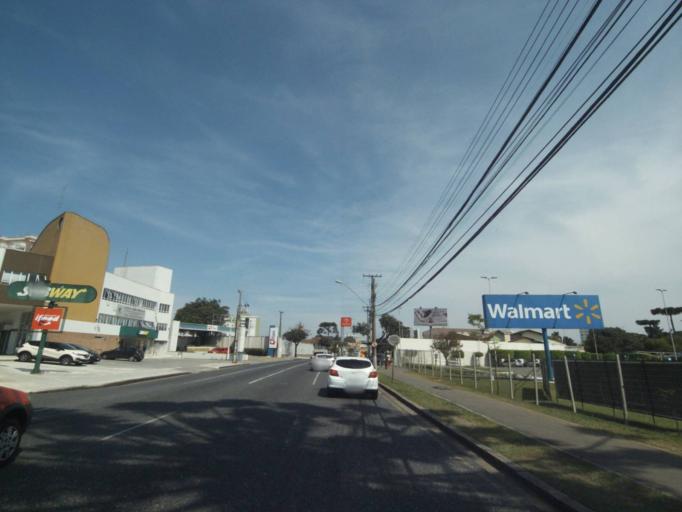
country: BR
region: Parana
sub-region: Curitiba
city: Curitiba
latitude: -25.4704
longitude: -49.2954
